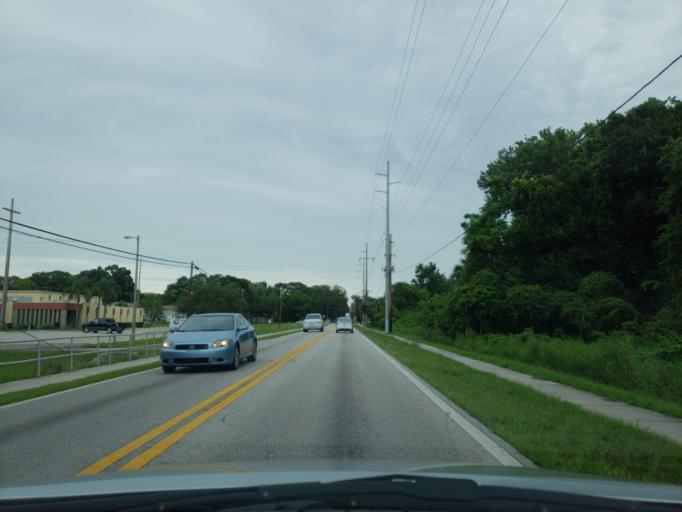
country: US
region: Florida
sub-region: Hillsborough County
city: Egypt Lake-Leto
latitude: 28.0002
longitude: -82.5009
